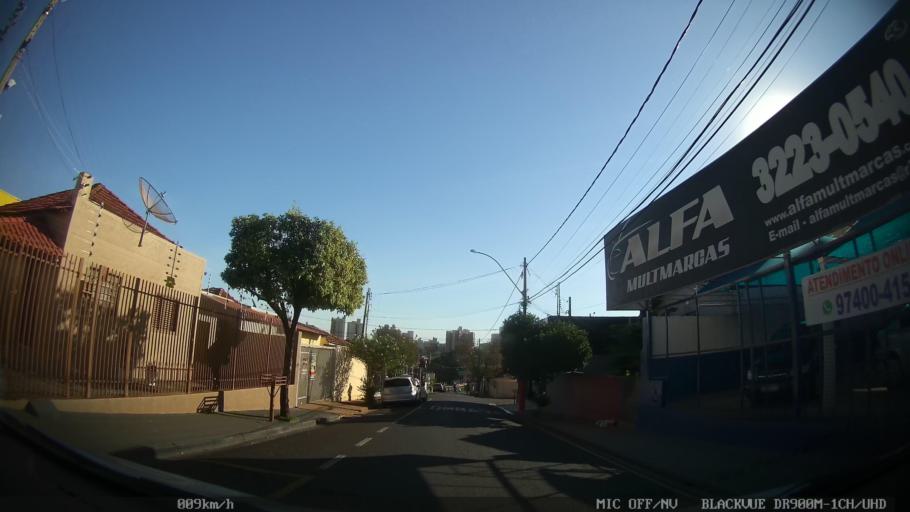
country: BR
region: Sao Paulo
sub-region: Sao Jose Do Rio Preto
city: Sao Jose do Rio Preto
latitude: -20.8036
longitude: -49.3751
